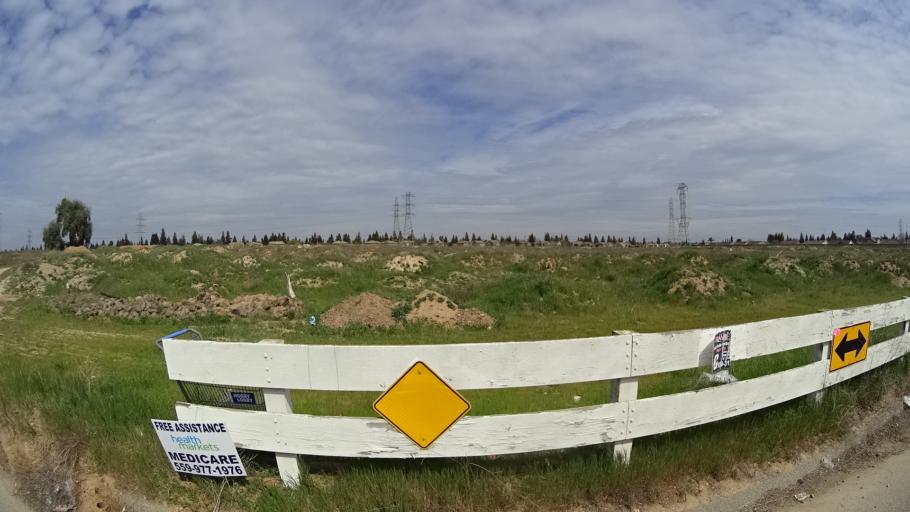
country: US
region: California
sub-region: Fresno County
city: Biola
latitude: 36.8342
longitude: -119.9002
